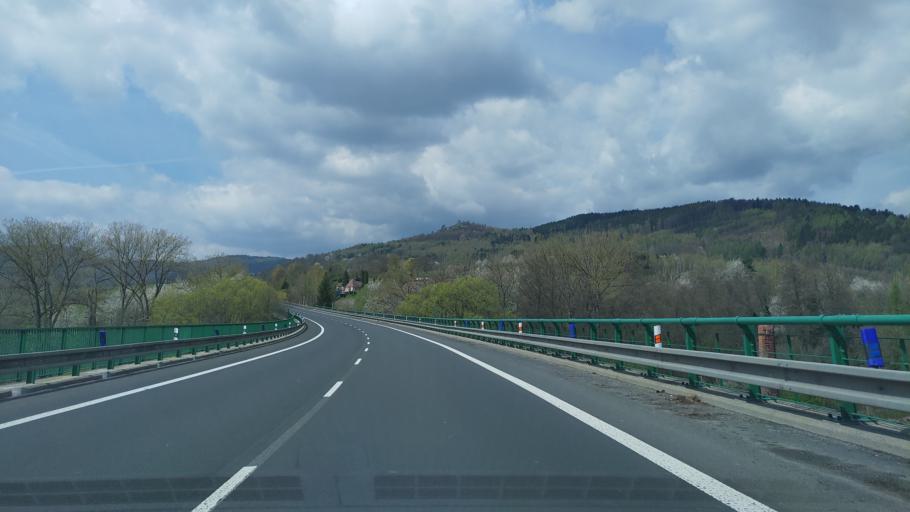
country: CZ
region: Ustecky
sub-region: Okres Chomutov
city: Perstejn
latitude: 50.3751
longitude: 13.1150
